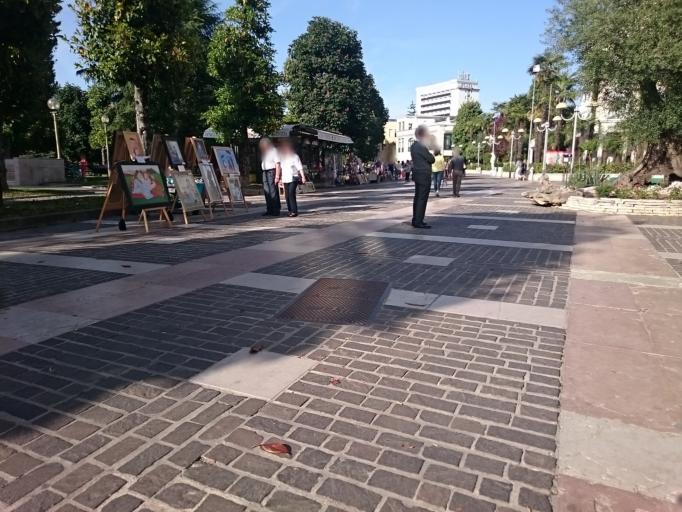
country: IT
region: Veneto
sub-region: Provincia di Padova
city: Abano Terme
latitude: 45.3524
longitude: 11.7805
